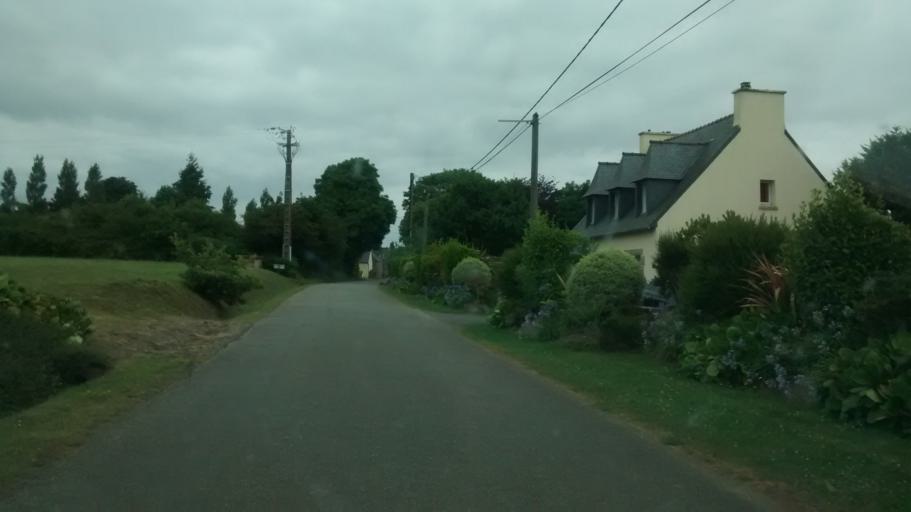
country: FR
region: Brittany
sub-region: Departement du Finistere
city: Lanveoc
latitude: 48.3344
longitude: -4.4311
